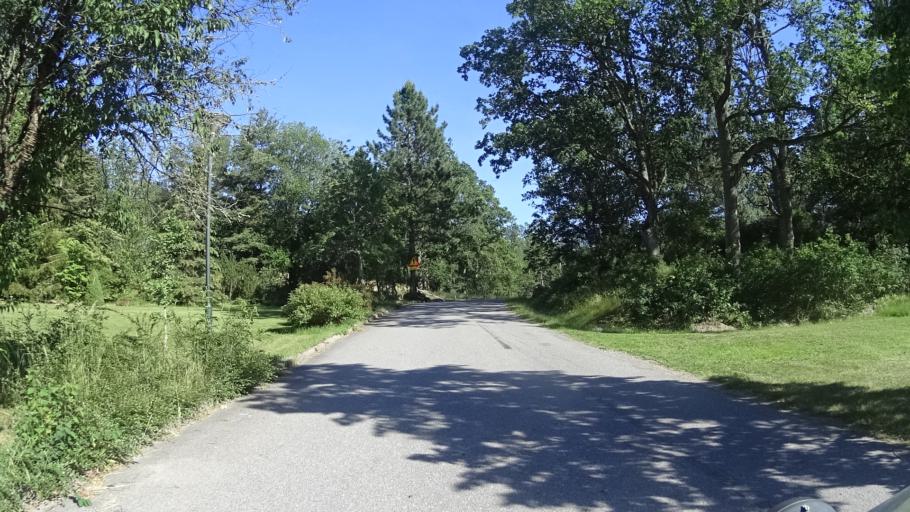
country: SE
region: Kalmar
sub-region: Vasterviks Kommun
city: Gamleby
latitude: 57.9100
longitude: 16.4079
